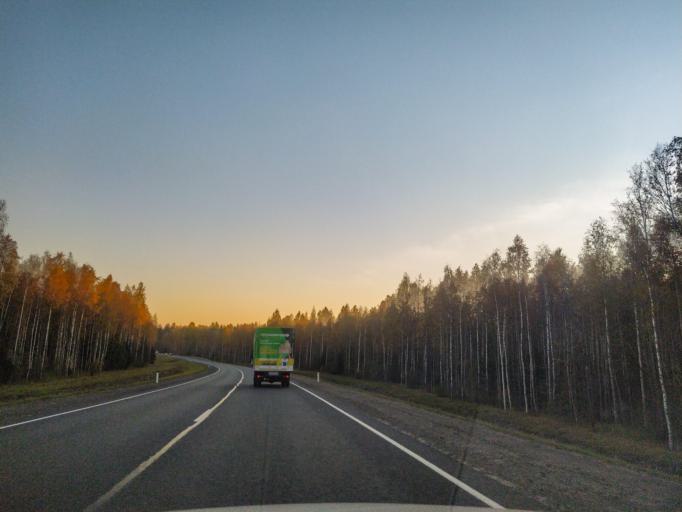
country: RU
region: Leningrad
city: Kuznechnoye
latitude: 61.2822
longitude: 29.7530
